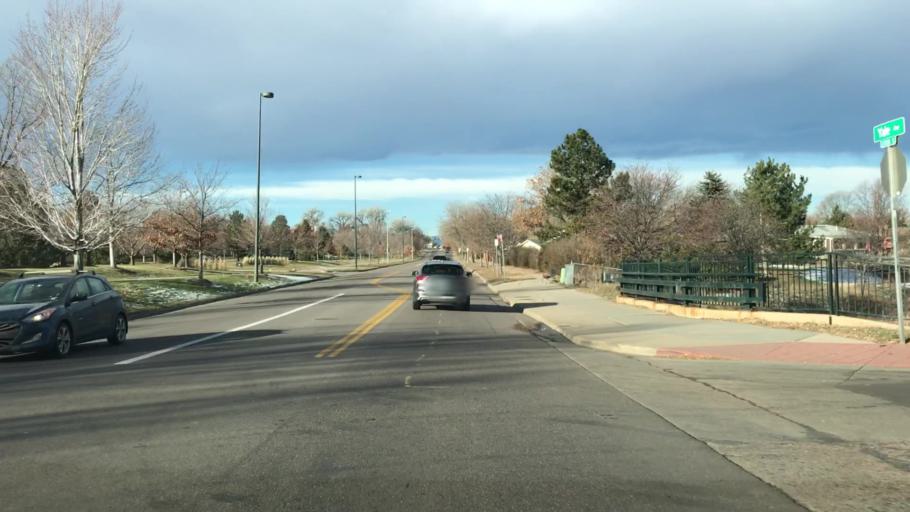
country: US
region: Colorado
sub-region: Arapahoe County
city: Glendale
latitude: 39.6677
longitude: -104.9060
